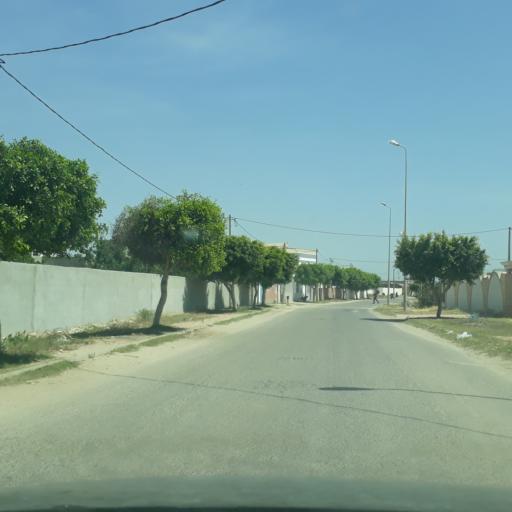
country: TN
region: Safaqis
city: Al Qarmadah
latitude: 34.8240
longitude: 10.7819
